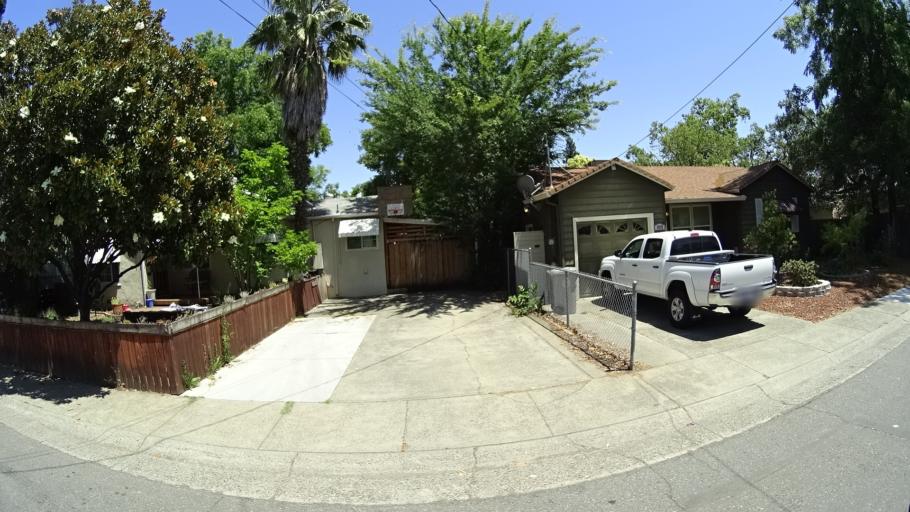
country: US
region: California
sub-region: Sacramento County
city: Parkway
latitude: 38.5400
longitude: -121.4439
